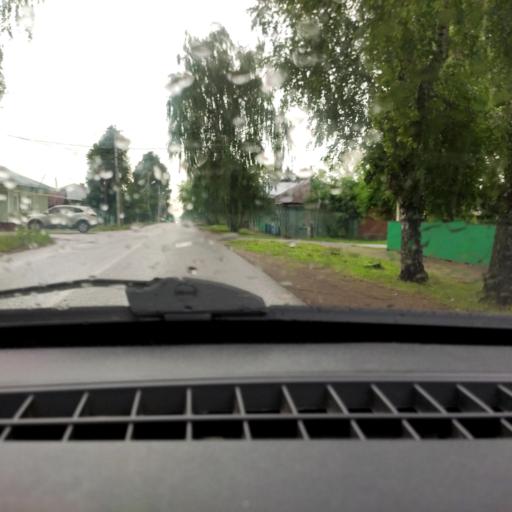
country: RU
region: Bashkortostan
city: Birsk
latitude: 55.4179
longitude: 55.5409
